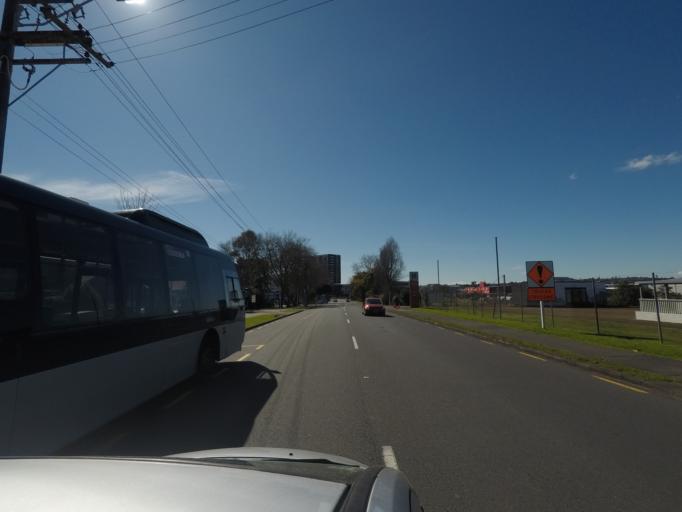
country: NZ
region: Auckland
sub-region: Auckland
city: Waitakere
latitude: -36.9126
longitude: 174.6819
